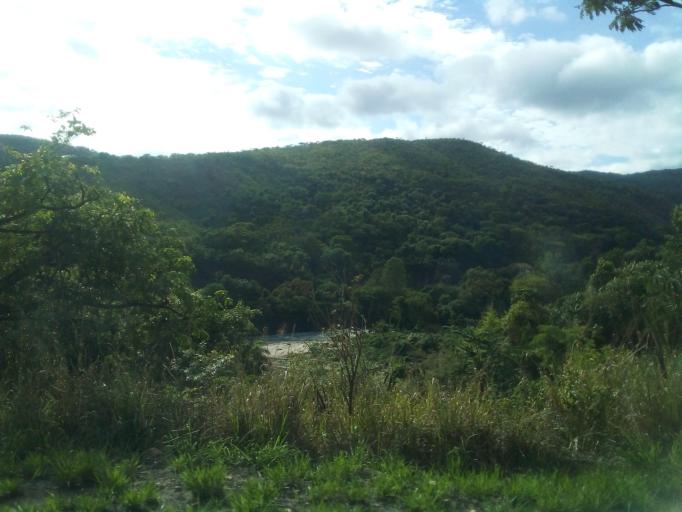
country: BR
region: Minas Gerais
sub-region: Belo Horizonte
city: Belo Horizonte
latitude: -19.8944
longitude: -43.8641
